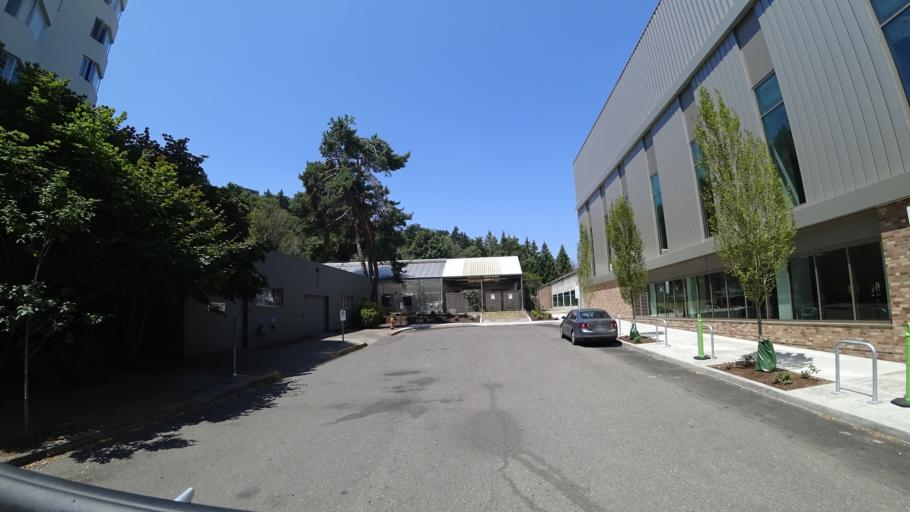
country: US
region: Oregon
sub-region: Multnomah County
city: Portland
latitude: 45.5105
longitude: -122.6865
